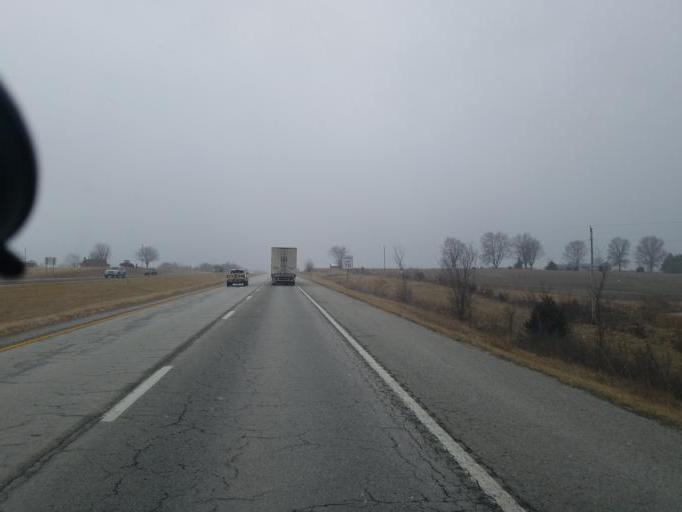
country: US
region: Missouri
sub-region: Macon County
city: La Plata
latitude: 39.9173
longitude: -92.4745
